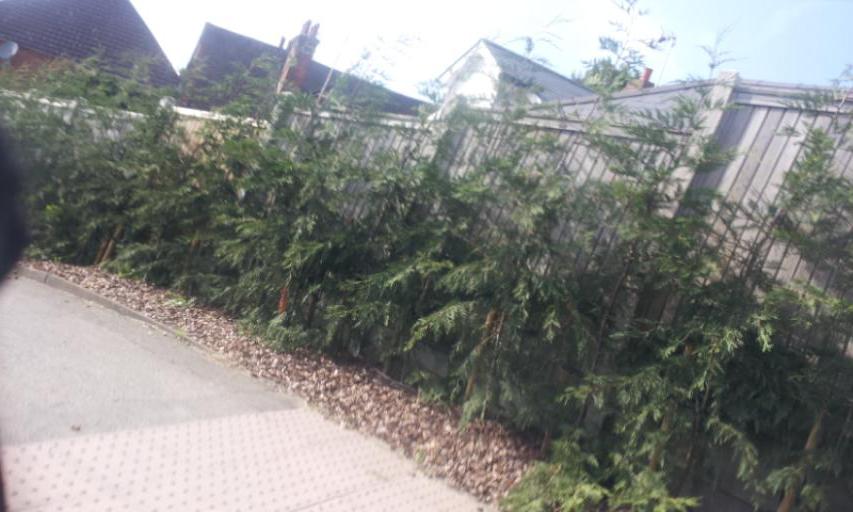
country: GB
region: England
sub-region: Kent
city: Harrietsham
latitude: 51.2420
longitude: 0.6757
